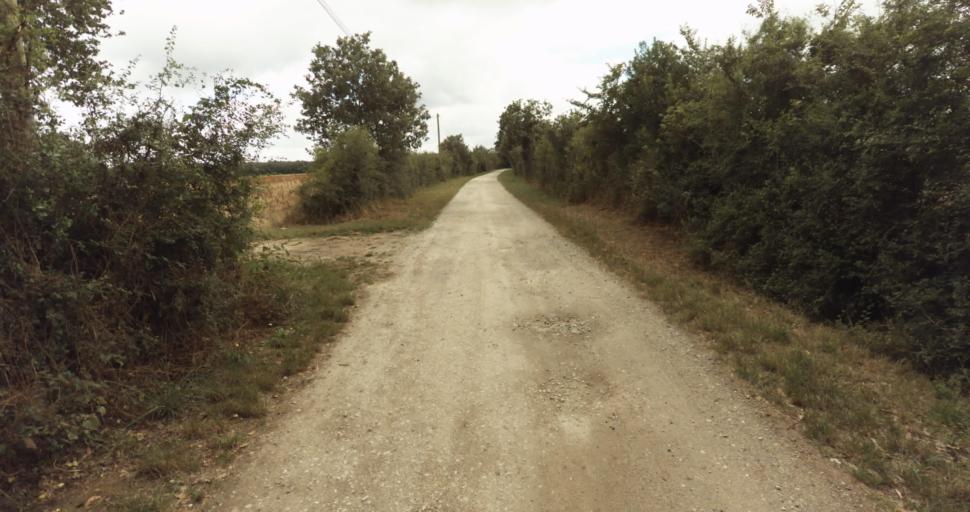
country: FR
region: Midi-Pyrenees
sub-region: Departement de la Haute-Garonne
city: Fonsorbes
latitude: 43.5548
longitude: 1.2365
